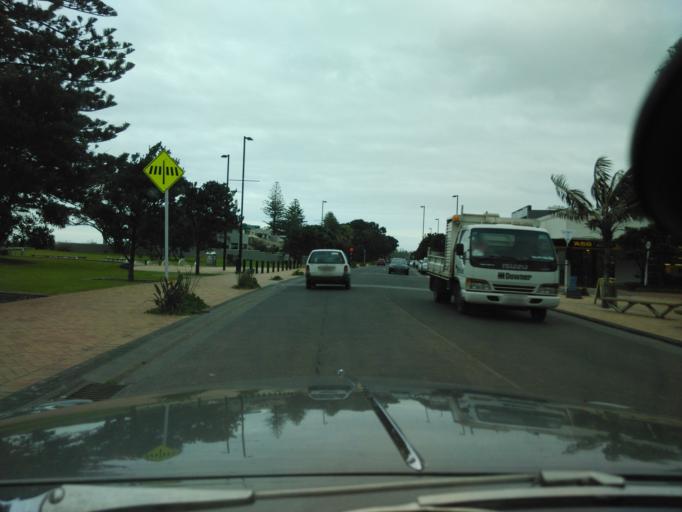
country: NZ
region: Auckland
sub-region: Auckland
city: Rothesay Bay
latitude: -36.5858
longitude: 174.6960
